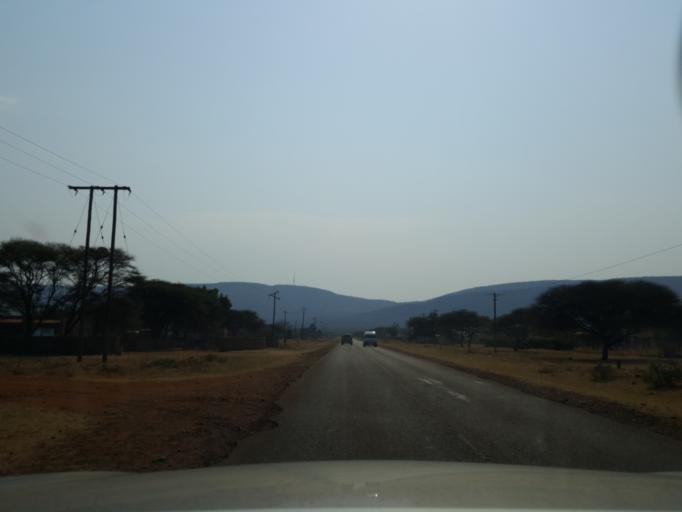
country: BW
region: South East
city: Lobatse
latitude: -25.2978
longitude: 25.8392
